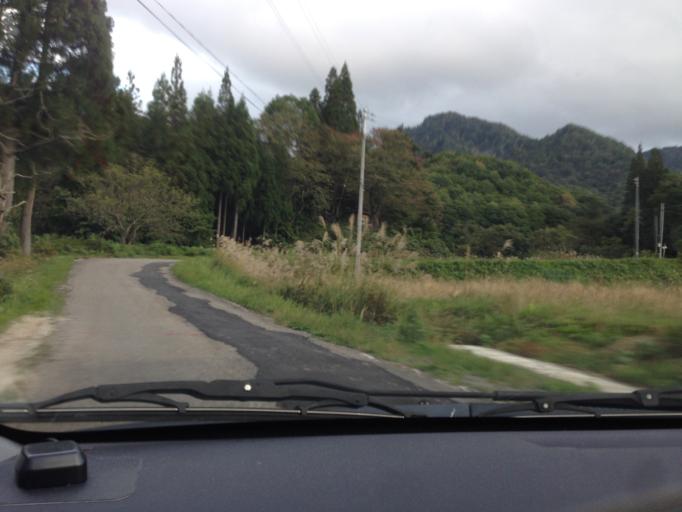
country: JP
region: Fukushima
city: Kitakata
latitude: 37.3917
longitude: 139.6115
